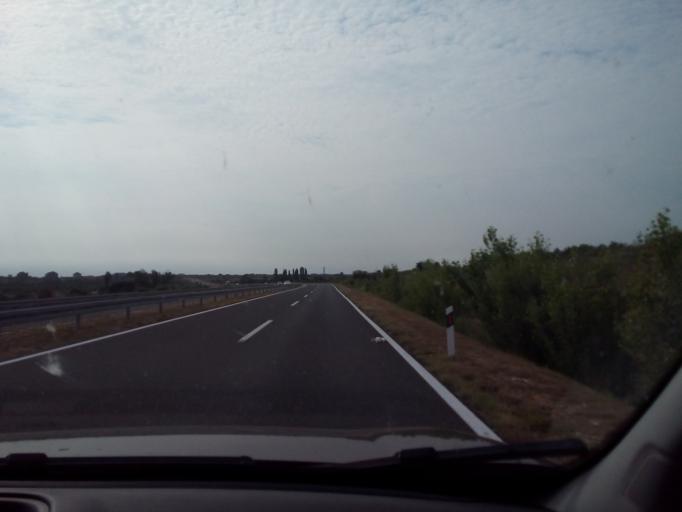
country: HR
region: Zadarska
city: Bibinje
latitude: 44.0967
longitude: 15.2939
